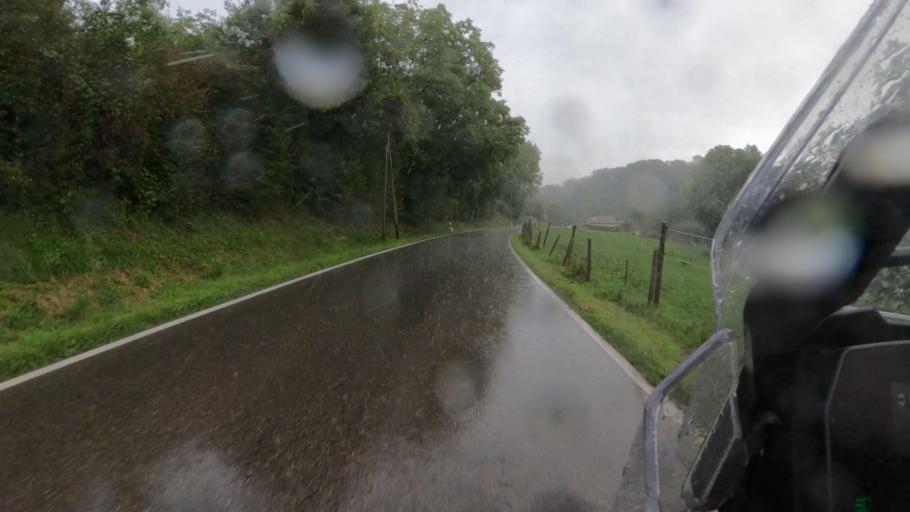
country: DE
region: Baden-Wuerttemberg
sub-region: Freiburg Region
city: Jestetten
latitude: 47.6477
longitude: 8.5726
